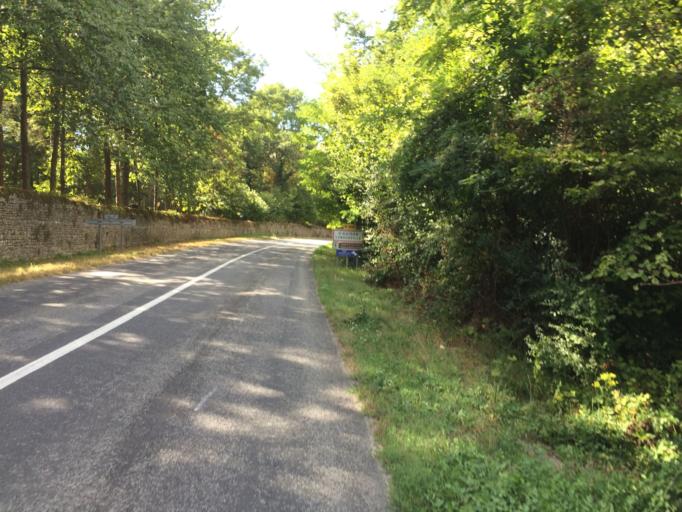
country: FR
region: Ile-de-France
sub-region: Departement de l'Essonne
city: Cerny
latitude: 48.4503
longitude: 2.3447
